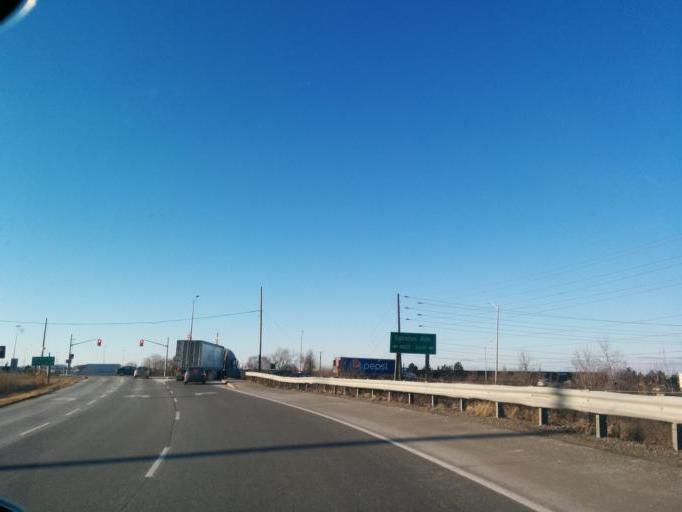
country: CA
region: Ontario
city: Mississauga
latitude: 43.6223
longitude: -79.6339
